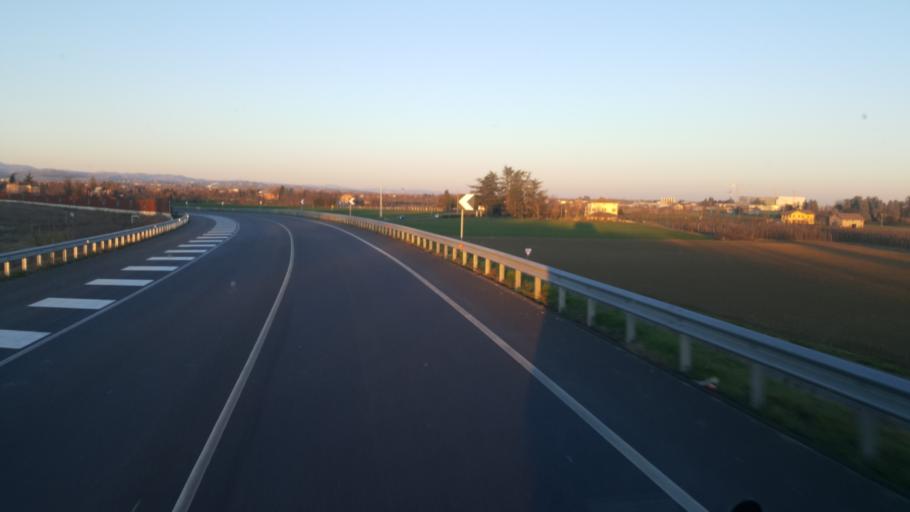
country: IT
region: Emilia-Romagna
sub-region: Provincia di Bologna
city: Bazzano
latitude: 44.5146
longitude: 11.0787
